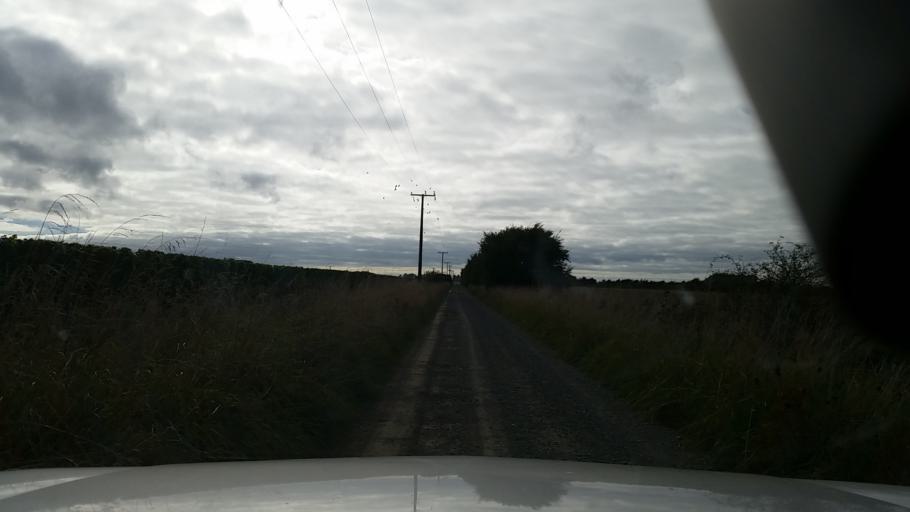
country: NZ
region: Marlborough
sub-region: Marlborough District
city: Blenheim
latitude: -41.4662
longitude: 173.9853
